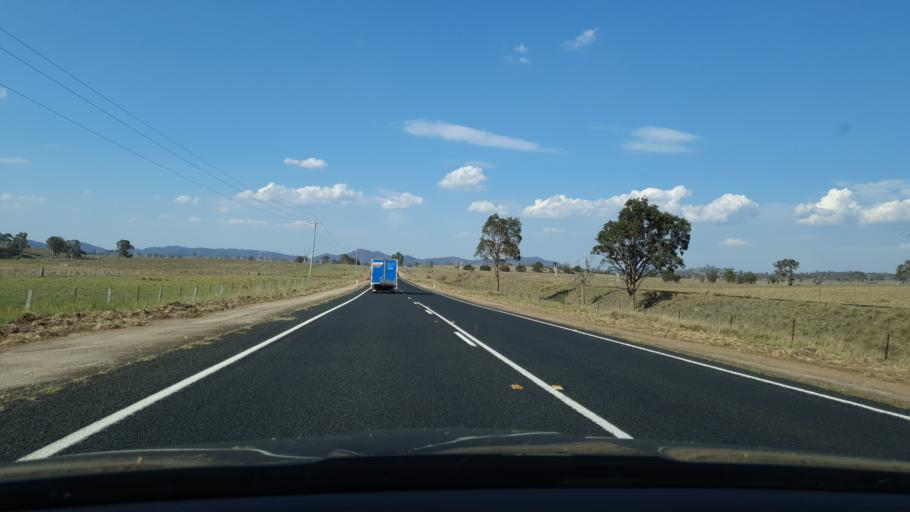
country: AU
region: New South Wales
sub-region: Glen Innes Severn
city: Glen Innes
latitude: -29.4201
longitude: 151.8618
